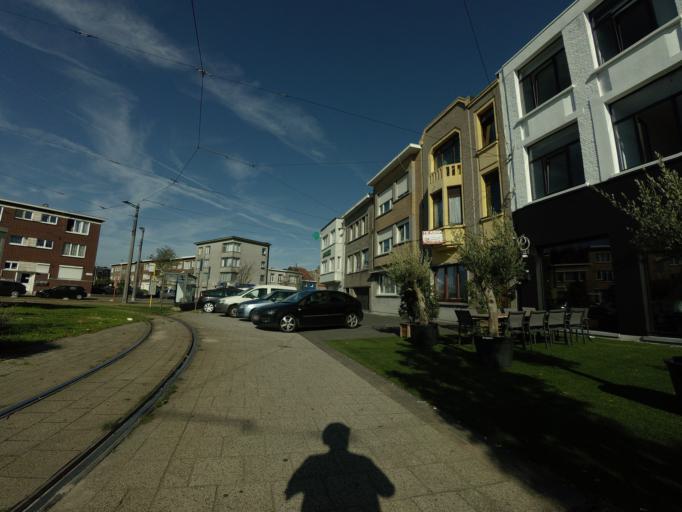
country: BE
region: Flanders
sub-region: Provincie Antwerpen
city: Borsbeek
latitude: 51.2192
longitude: 4.4754
